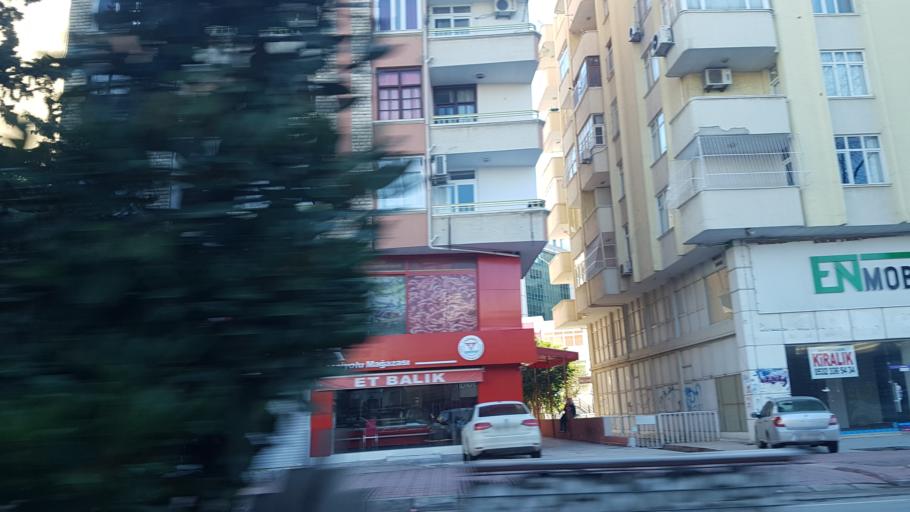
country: TR
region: Adana
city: Adana
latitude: 37.0190
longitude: 35.3165
